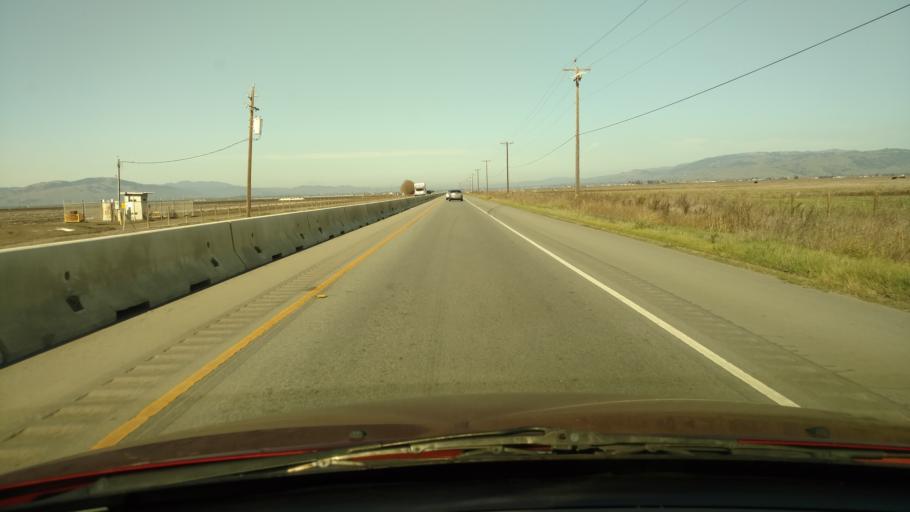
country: US
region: California
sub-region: San Benito County
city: Hollister
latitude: 36.9126
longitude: -121.4438
